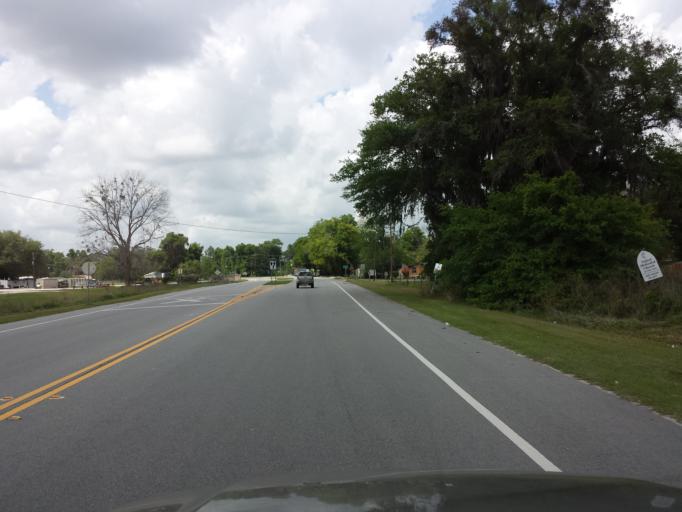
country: US
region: Georgia
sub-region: Echols County
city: Statenville
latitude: 30.6818
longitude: -83.1766
